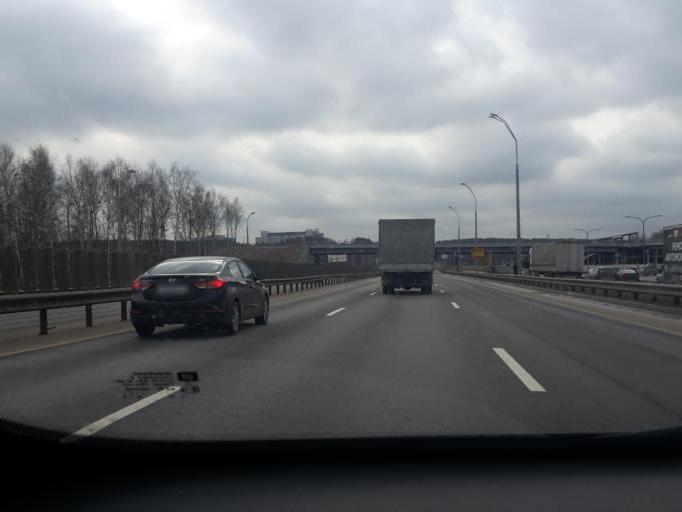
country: BY
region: Minsk
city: Borovlyany
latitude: 53.9386
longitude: 27.6764
